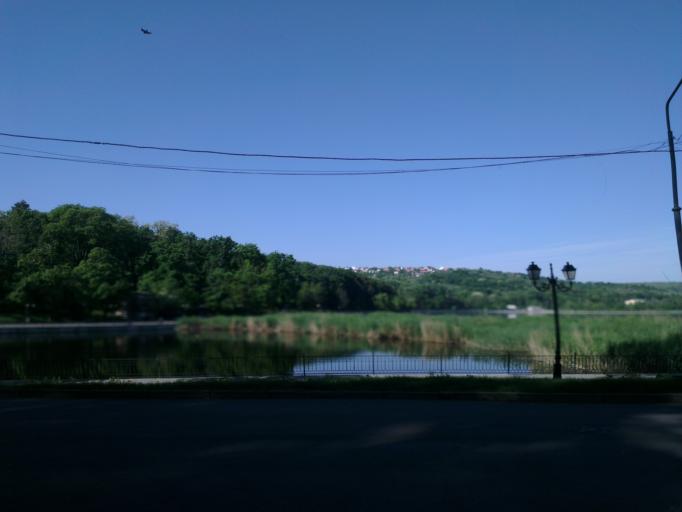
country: MD
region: Chisinau
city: Chisinau
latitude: 47.0191
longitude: 28.8185
